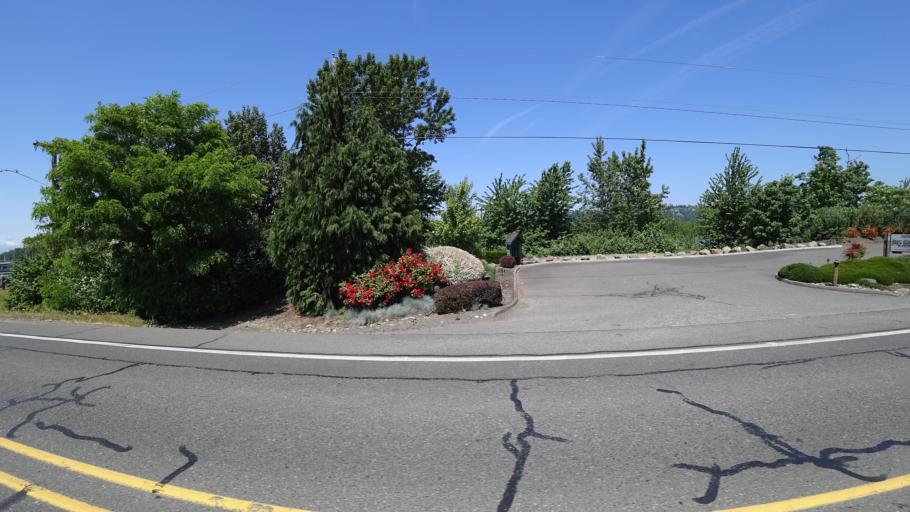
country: US
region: Oregon
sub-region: Multnomah County
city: Fairview
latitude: 45.5580
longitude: -122.4646
